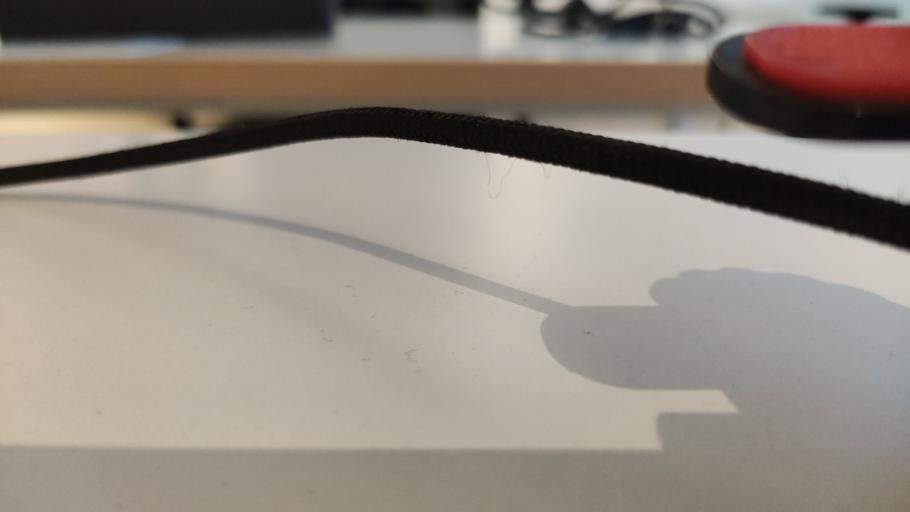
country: RU
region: Moskovskaya
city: Sychevo
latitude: 55.8245
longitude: 36.3117
